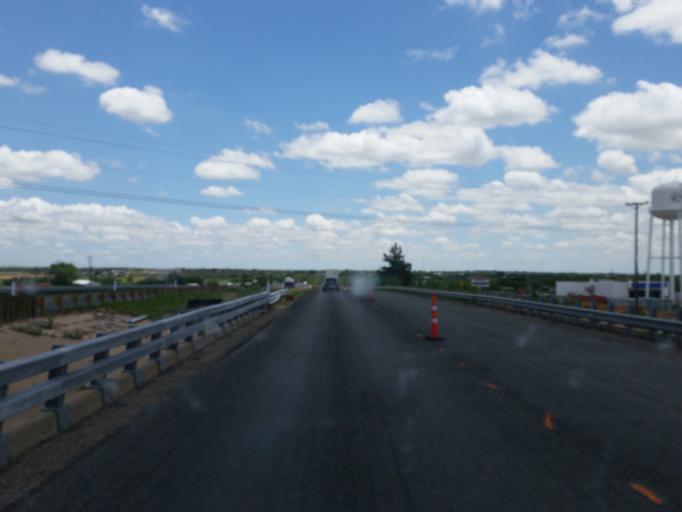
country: US
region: Texas
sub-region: Scurry County
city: Snyder
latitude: 32.7391
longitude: -100.9184
